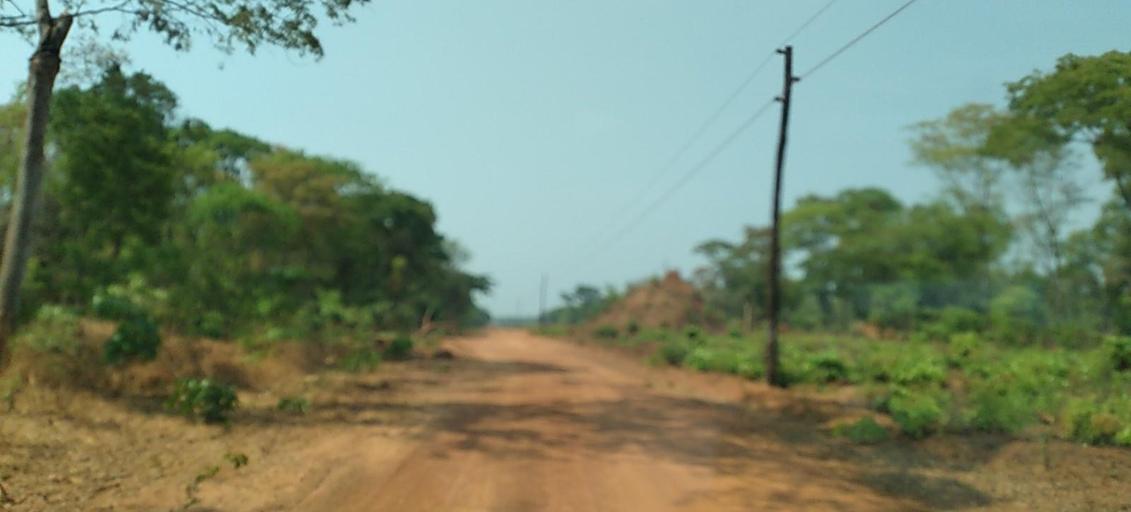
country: ZM
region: Copperbelt
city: Kalulushi
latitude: -13.0816
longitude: 27.4108
